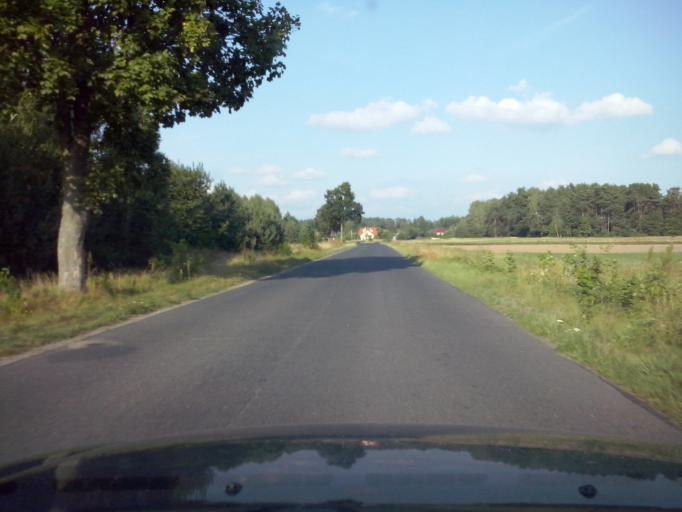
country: PL
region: Subcarpathian Voivodeship
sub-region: Powiat lezajski
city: Wola Zarczycka
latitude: 50.3043
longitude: 22.2957
